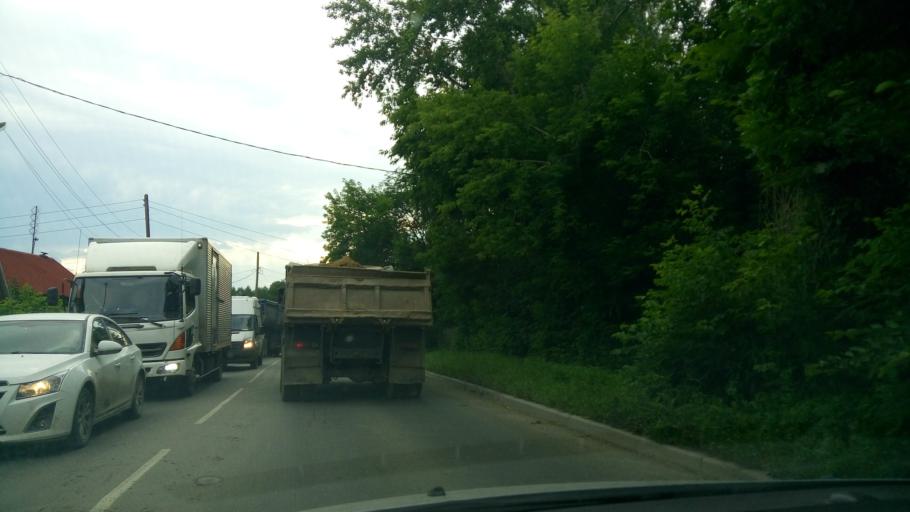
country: RU
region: Sverdlovsk
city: Yekaterinburg
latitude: 56.8819
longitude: 60.6919
